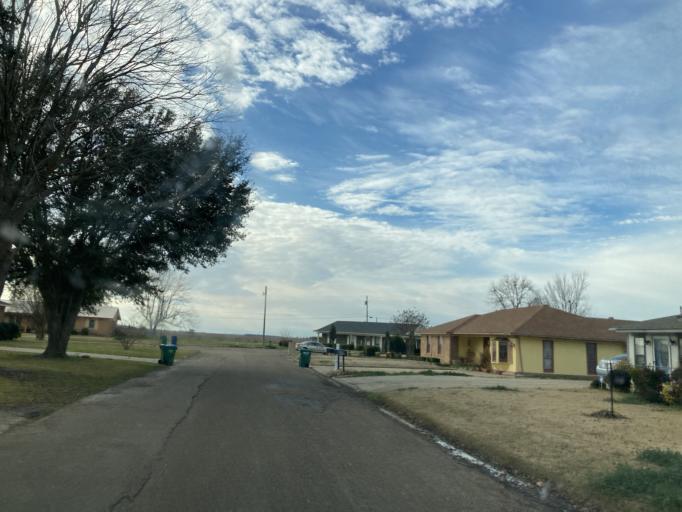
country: US
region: Mississippi
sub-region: Humphreys County
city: Belzoni
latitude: 33.1721
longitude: -90.5031
